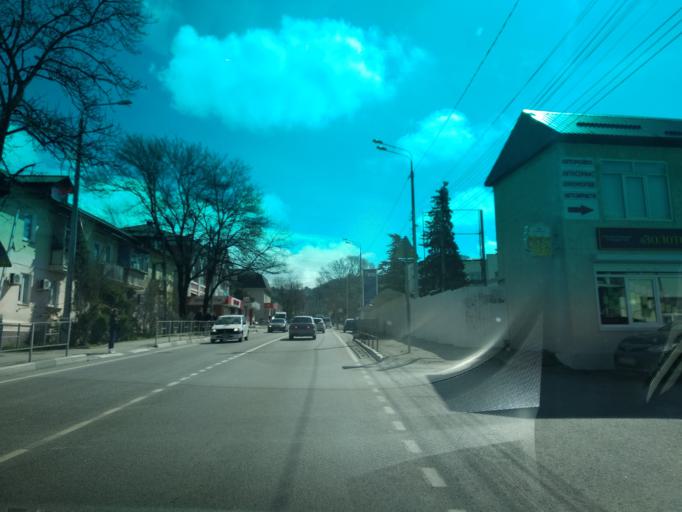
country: RU
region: Krasnodarskiy
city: Tuapse
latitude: 44.0990
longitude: 39.0968
